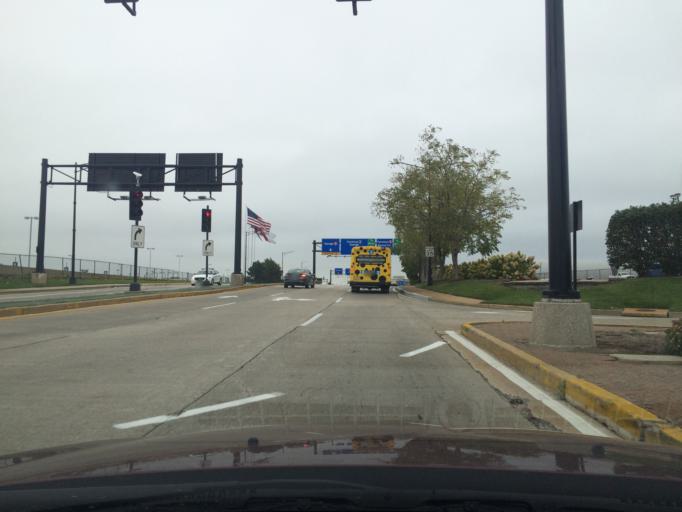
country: US
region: Missouri
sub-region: Saint Louis County
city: Woodson Terrace
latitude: 38.7420
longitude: -90.3690
